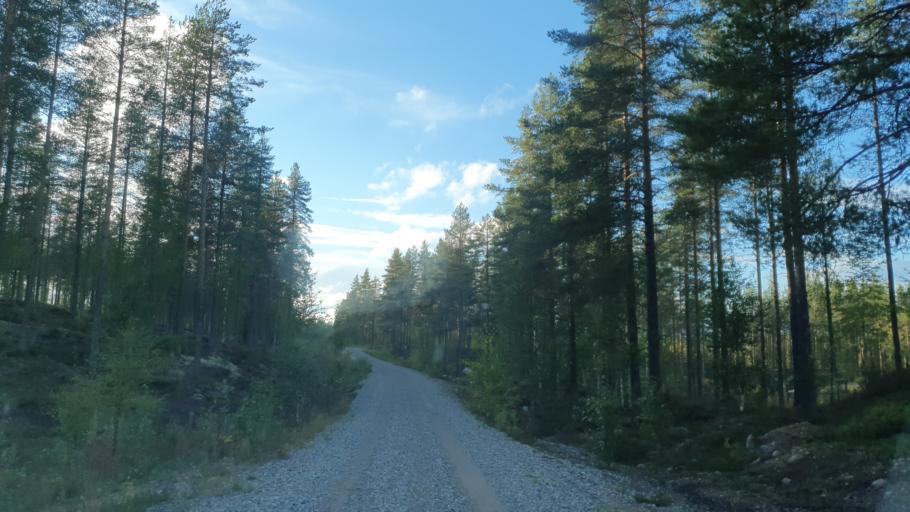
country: FI
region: Kainuu
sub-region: Kehys-Kainuu
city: Kuhmo
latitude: 64.3365
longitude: 29.9916
